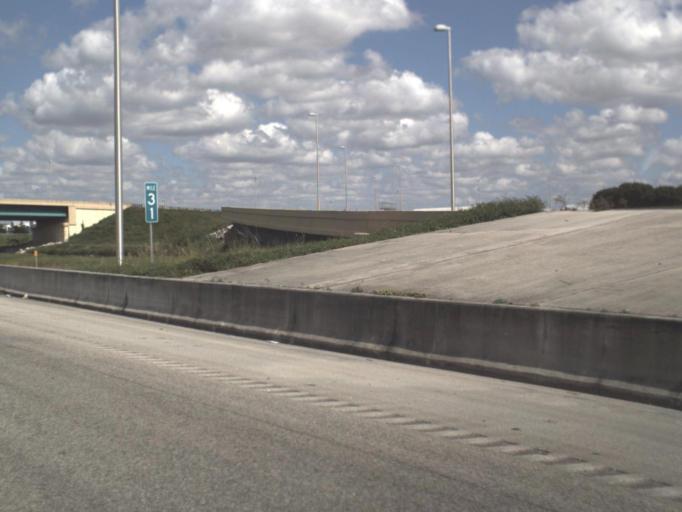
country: US
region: Florida
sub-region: Miami-Dade County
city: Doral
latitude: 25.8385
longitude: -80.3869
